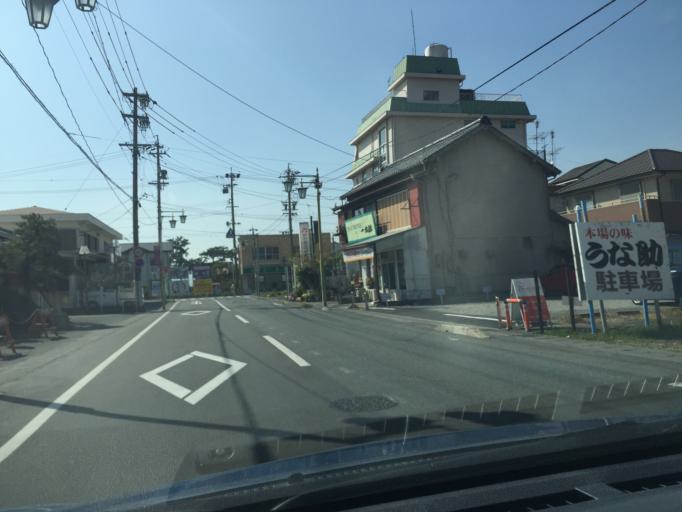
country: JP
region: Shizuoka
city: Kosai-shi
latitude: 34.7642
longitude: 137.6144
